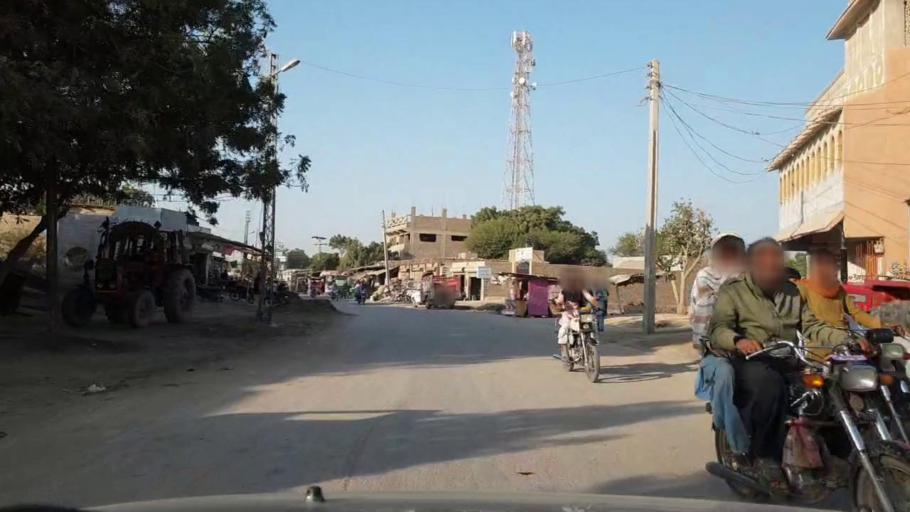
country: PK
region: Sindh
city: Chambar
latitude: 25.2891
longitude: 68.8120
